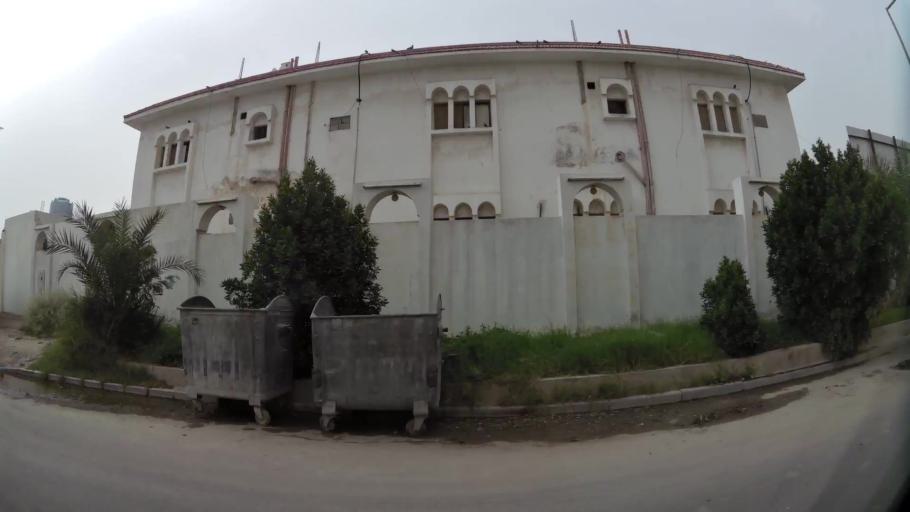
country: QA
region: Baladiyat ad Dawhah
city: Doha
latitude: 25.2493
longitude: 51.5124
